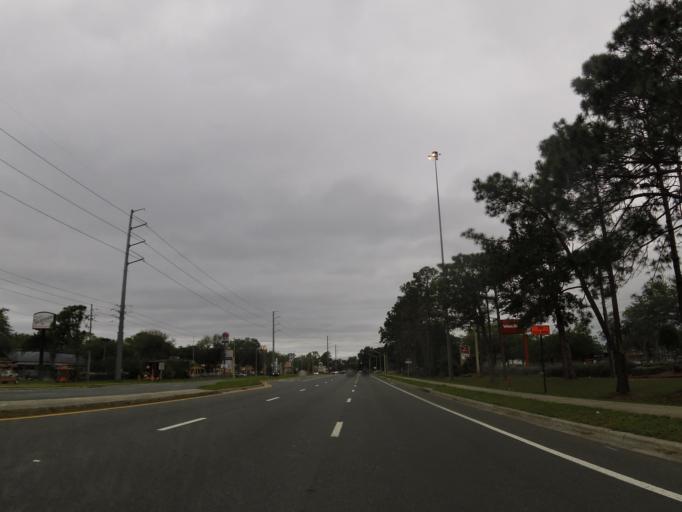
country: US
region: Florida
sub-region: Saint Johns County
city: Fruit Cove
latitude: 30.1711
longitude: -81.6029
